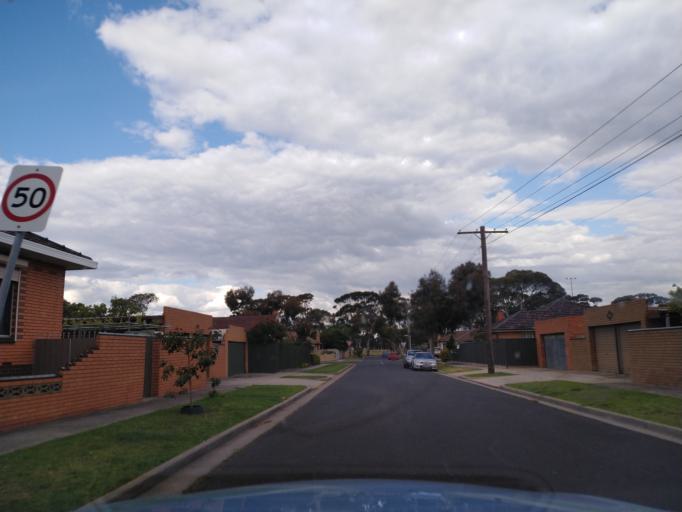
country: AU
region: Victoria
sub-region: Hobsons Bay
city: Altona North
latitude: -37.8407
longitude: 144.8530
